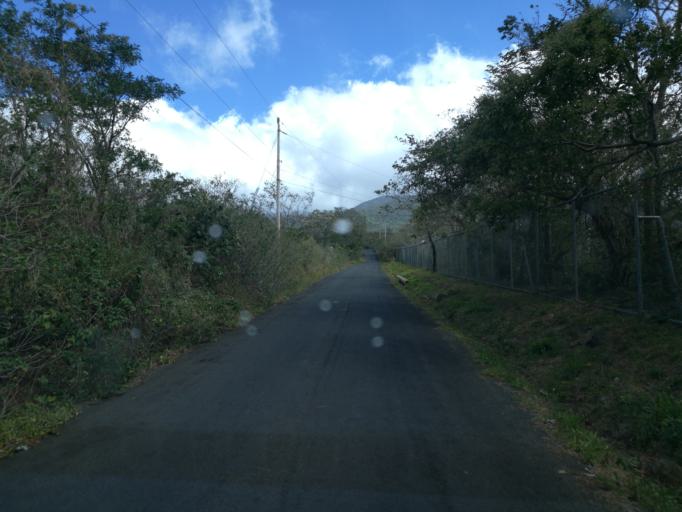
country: CR
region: Guanacaste
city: Liberia
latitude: 10.7704
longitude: -85.3507
